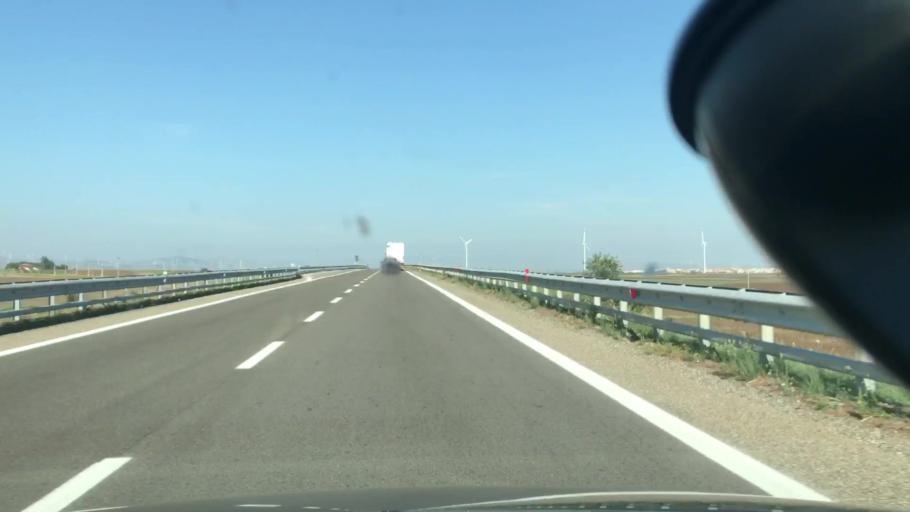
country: IT
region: Basilicate
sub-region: Provincia di Potenza
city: Lavello
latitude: 41.0144
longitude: 15.8253
